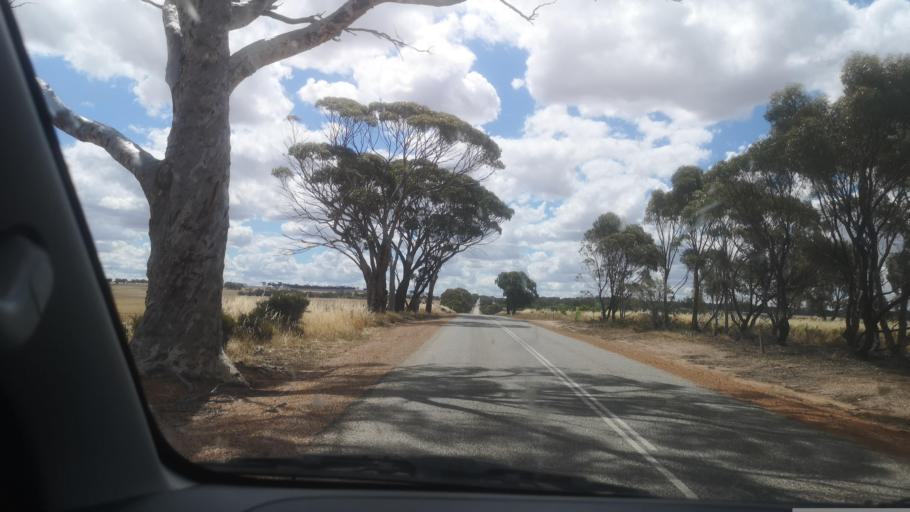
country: AU
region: Western Australia
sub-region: Beverley
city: Beverley
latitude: -31.9747
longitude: 117.0791
